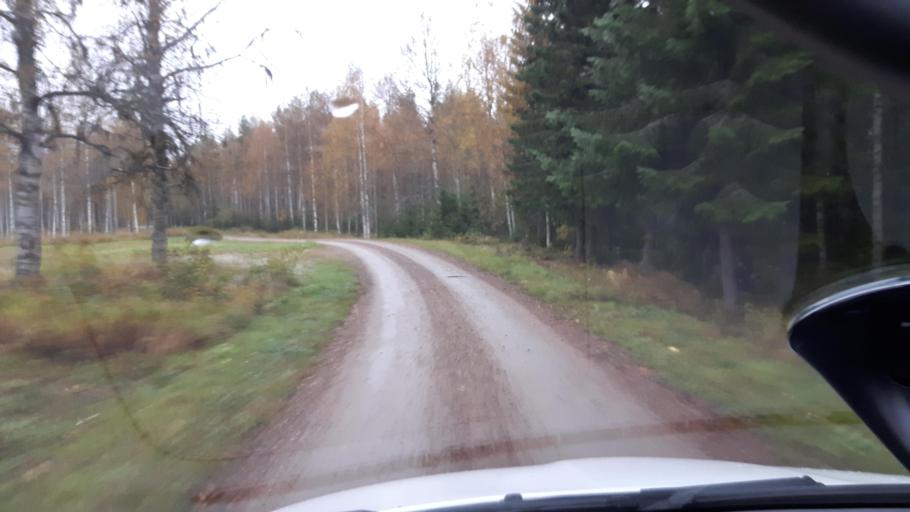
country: SE
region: Vaesternorrland
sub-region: Ange Kommun
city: Ange
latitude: 62.1822
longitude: 15.6294
